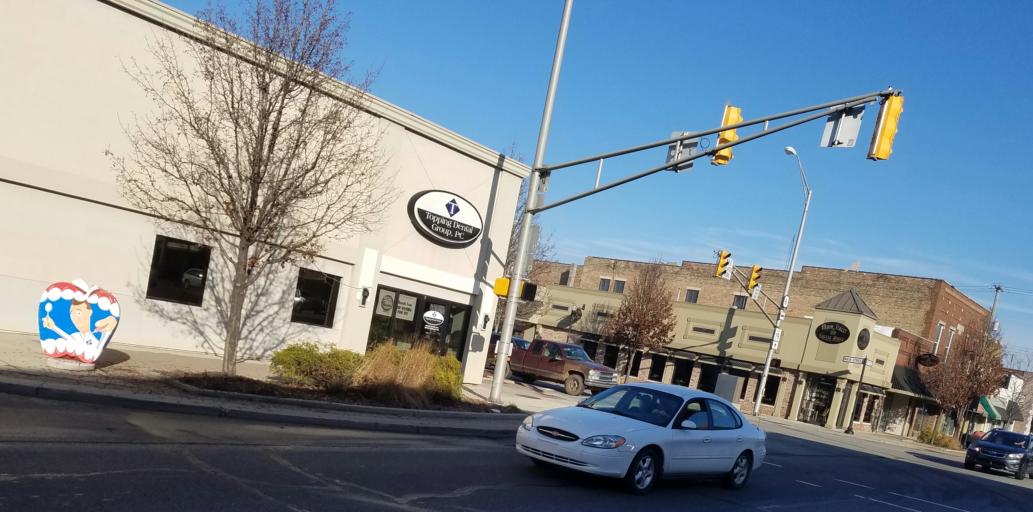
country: US
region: Indiana
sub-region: Elkhart County
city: Nappanee
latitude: 41.4426
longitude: -86.0017
